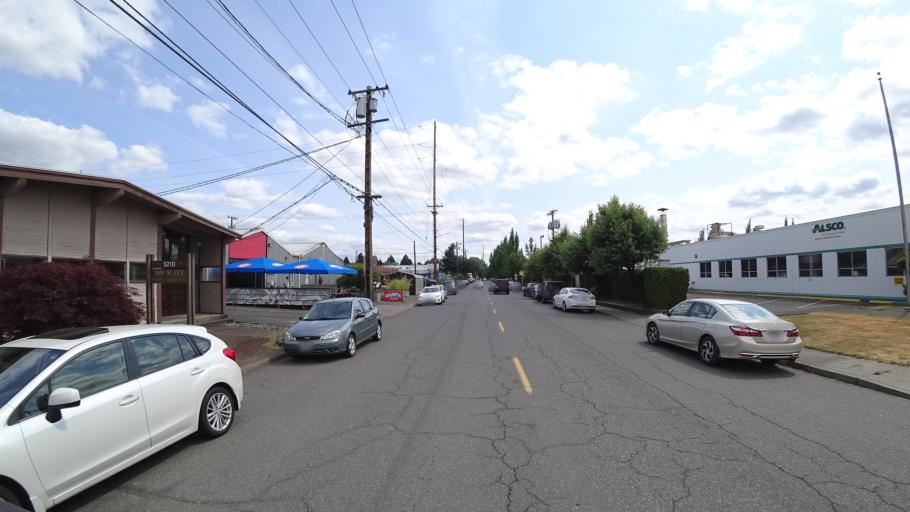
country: US
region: Oregon
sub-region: Clackamas County
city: Milwaukie
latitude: 45.4852
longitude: -122.6397
